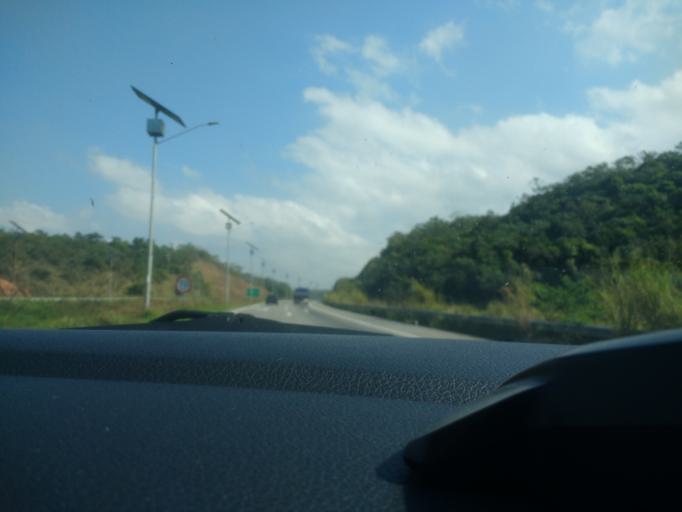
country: BR
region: Rio de Janeiro
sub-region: Queimados
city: Queimados
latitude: -22.6879
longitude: -43.4975
